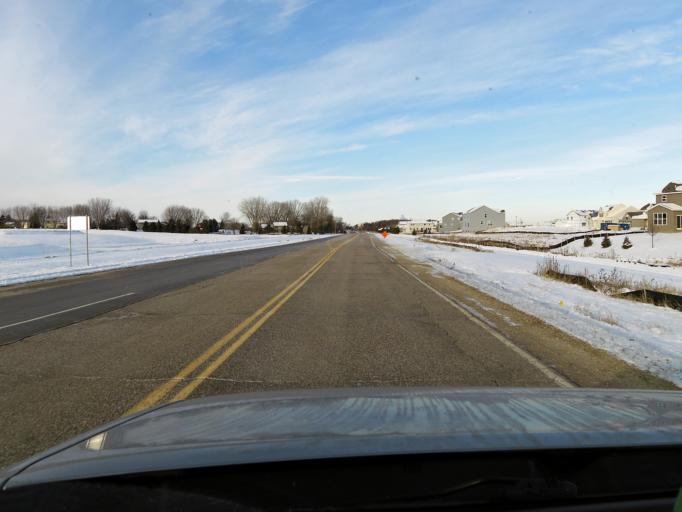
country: US
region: Minnesota
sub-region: Scott County
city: Prior Lake
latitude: 44.7647
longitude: -93.4157
